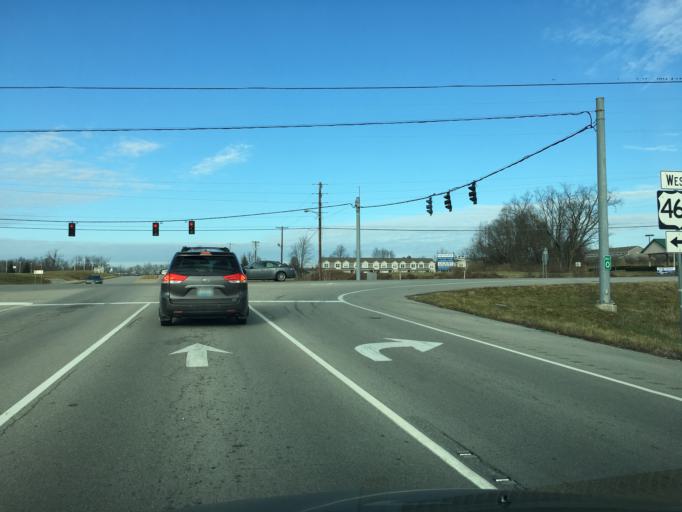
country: US
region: Kentucky
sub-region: Scott County
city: Georgetown
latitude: 38.2086
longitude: -84.5961
